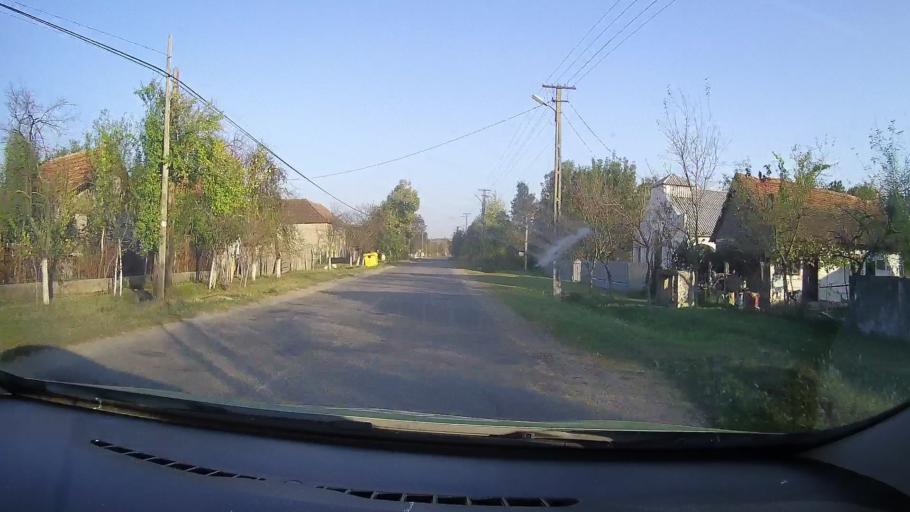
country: RO
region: Arad
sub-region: Comuna Silindia
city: Silindia
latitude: 46.3387
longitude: 21.9199
